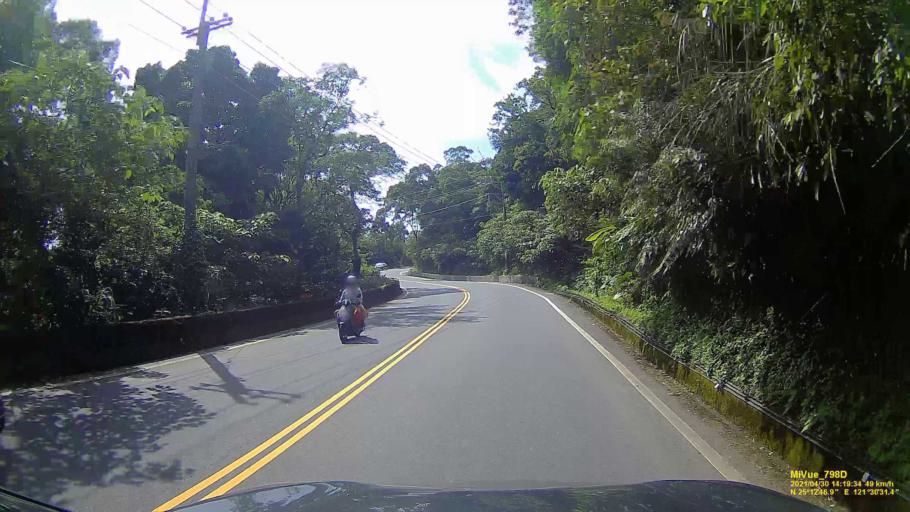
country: TW
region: Taipei
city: Taipei
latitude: 25.2131
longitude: 121.5085
